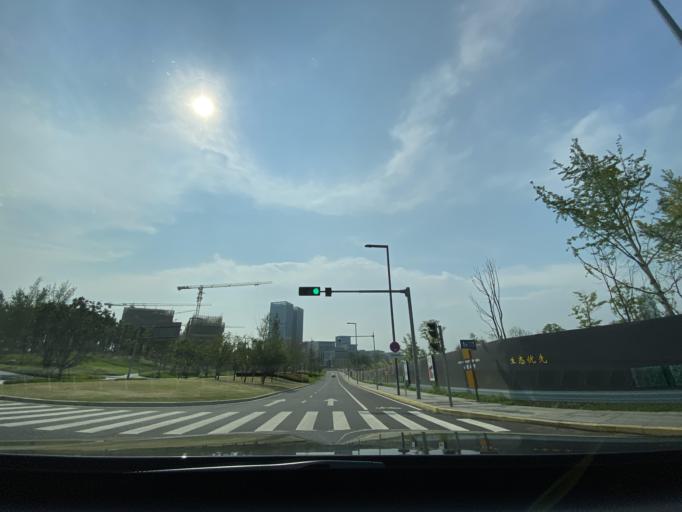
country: CN
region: Sichuan
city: Dongsheng
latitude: 30.3943
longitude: 104.0777
